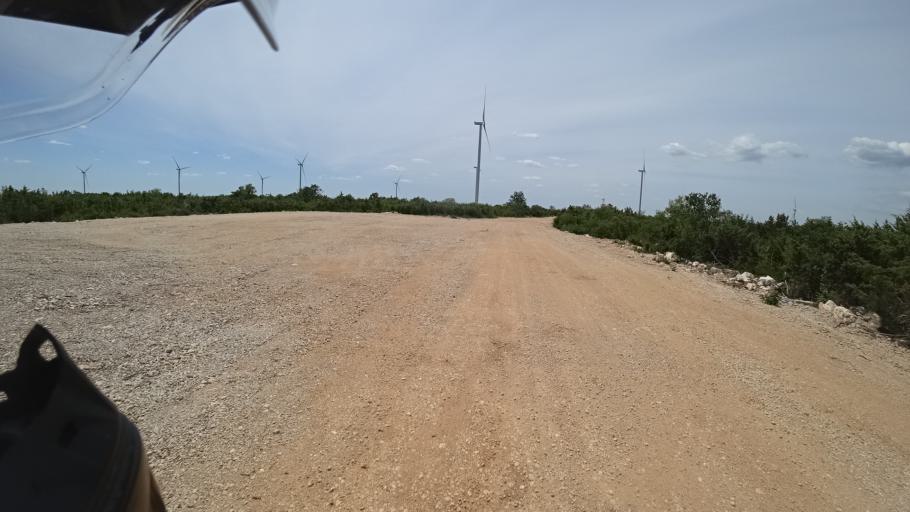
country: HR
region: Sibensko-Kniniska
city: Knin
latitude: 44.0649
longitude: 16.0963
